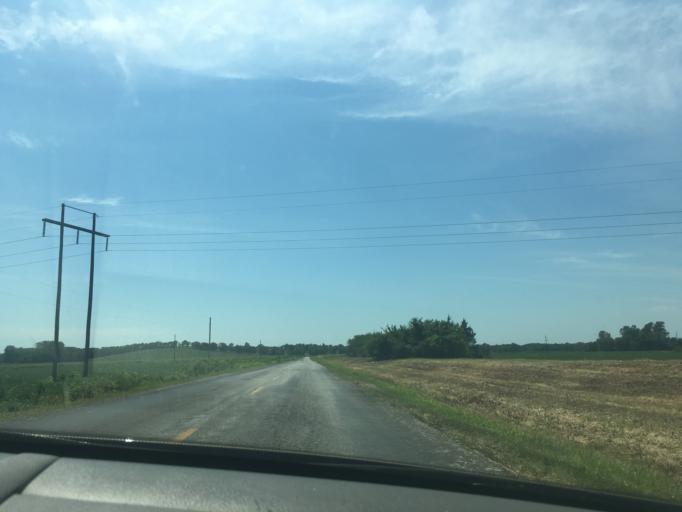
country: US
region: Missouri
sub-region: Gentry County
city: Stanberry
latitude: 40.2383
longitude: -94.7101
